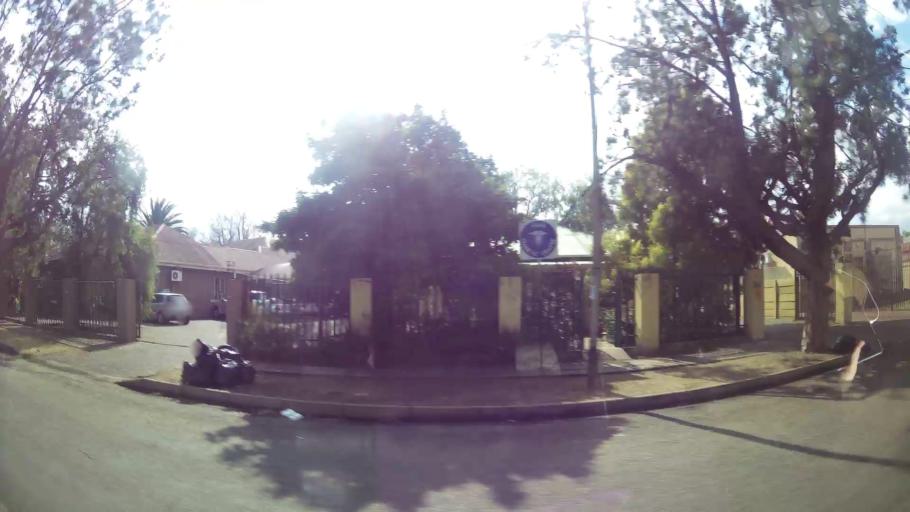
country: ZA
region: Gauteng
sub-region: Sedibeng District Municipality
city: Vereeniging
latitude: -26.6676
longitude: 27.9293
